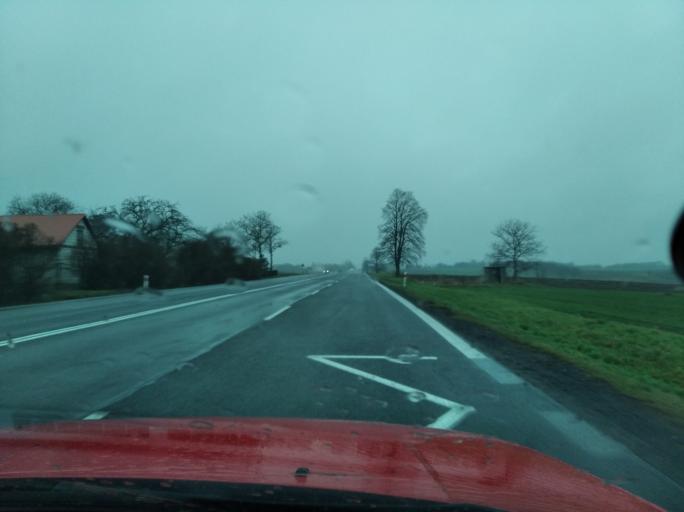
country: PL
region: Subcarpathian Voivodeship
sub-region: Powiat lancucki
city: Rogozno
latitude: 50.0671
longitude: 22.3893
